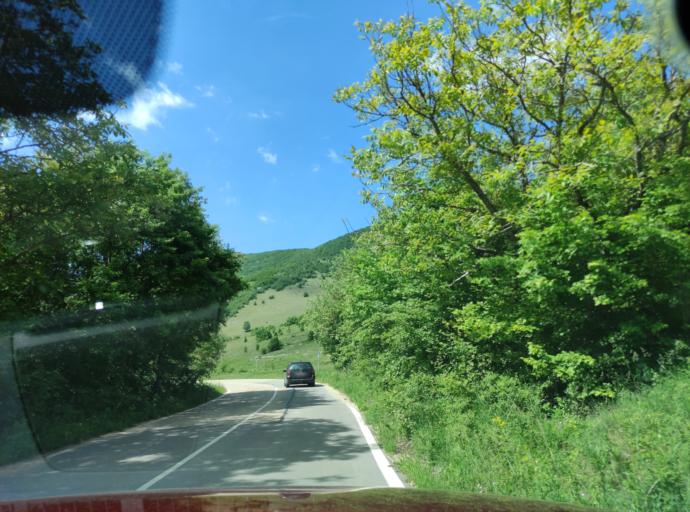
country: BG
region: Montana
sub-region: Obshtina Chiprovtsi
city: Chiprovtsi
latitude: 43.4871
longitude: 22.8146
